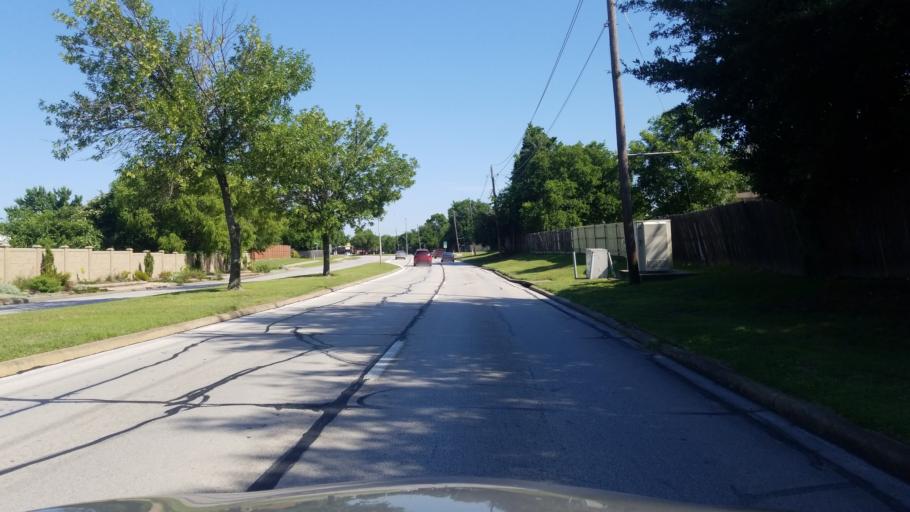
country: US
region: Texas
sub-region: Dallas County
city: Grand Prairie
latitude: 32.6889
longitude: -97.0152
